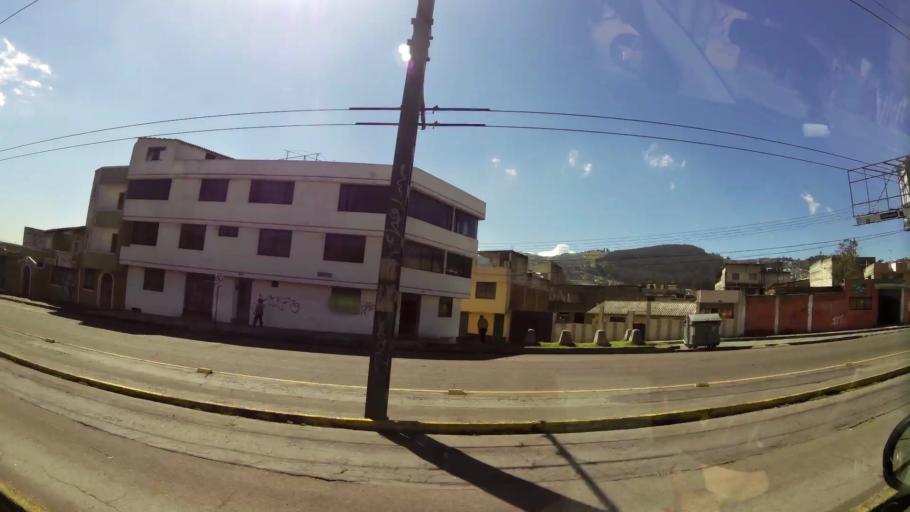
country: EC
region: Pichincha
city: Quito
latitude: -0.2625
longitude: -78.5306
